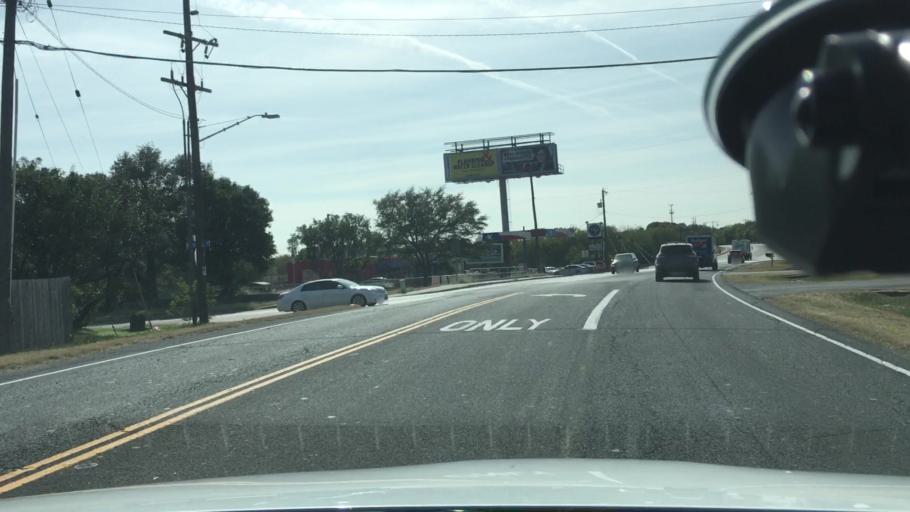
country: US
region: Texas
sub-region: Bexar County
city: Windcrest
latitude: 29.5727
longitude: -98.4182
